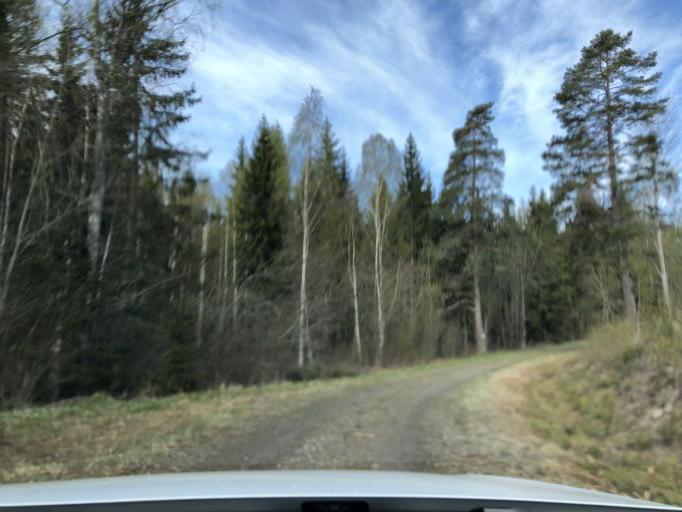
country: SE
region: Uppsala
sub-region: Heby Kommun
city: Tarnsjo
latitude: 60.2928
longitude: 16.8189
